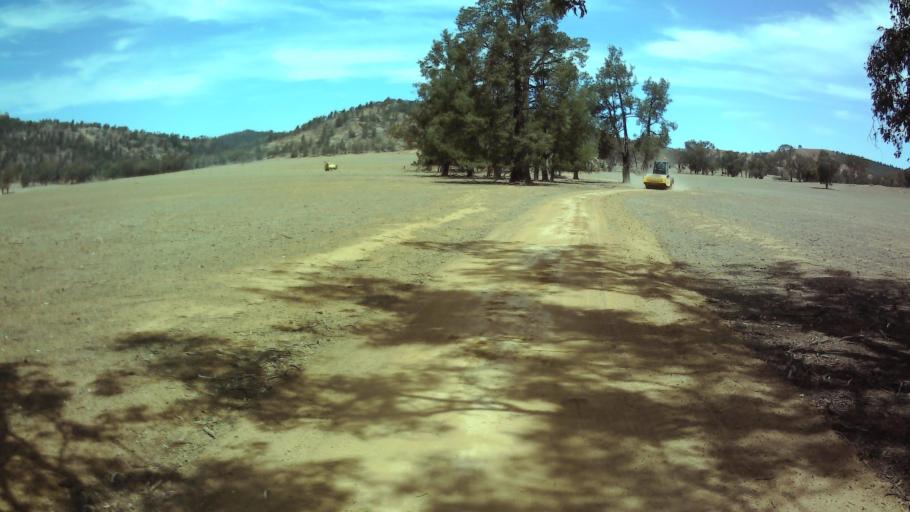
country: AU
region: New South Wales
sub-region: Weddin
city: Grenfell
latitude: -33.7716
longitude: 148.1509
